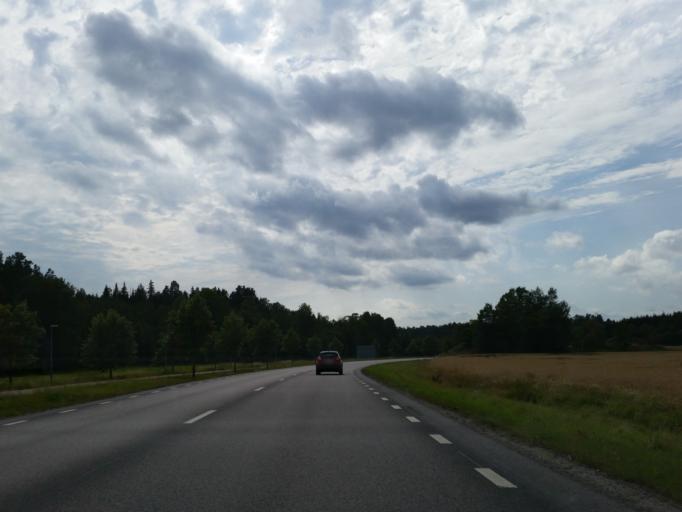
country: SE
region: Soedermanland
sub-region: Strangnas Kommun
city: Mariefred
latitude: 59.2520
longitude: 17.1752
